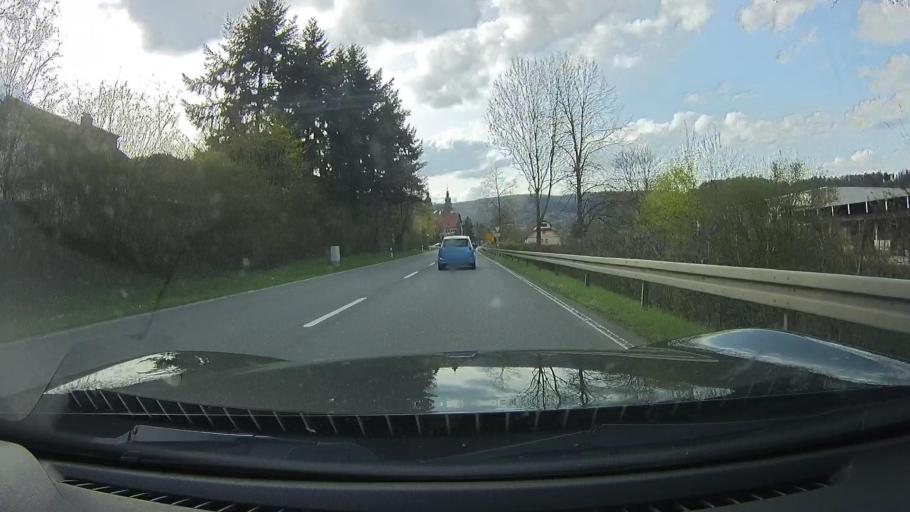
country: DE
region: Bavaria
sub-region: Regierungsbezirk Unterfranken
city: Weilbach
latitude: 49.6441
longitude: 9.2265
